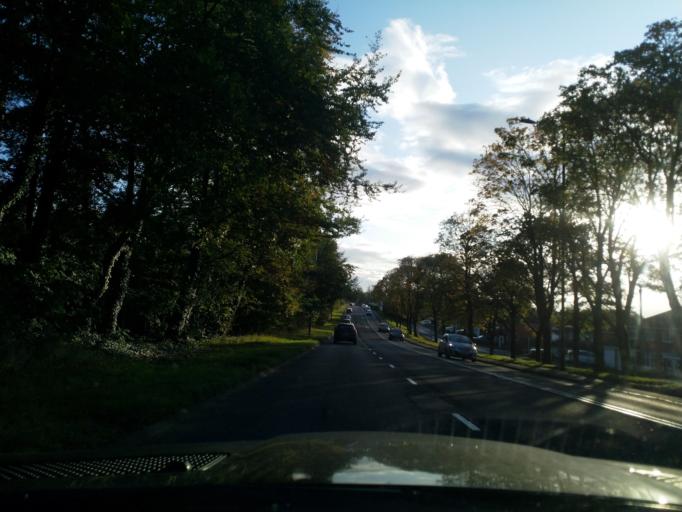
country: GB
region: England
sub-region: Worcestershire
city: Alvechurch
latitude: 52.3919
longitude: -1.9550
